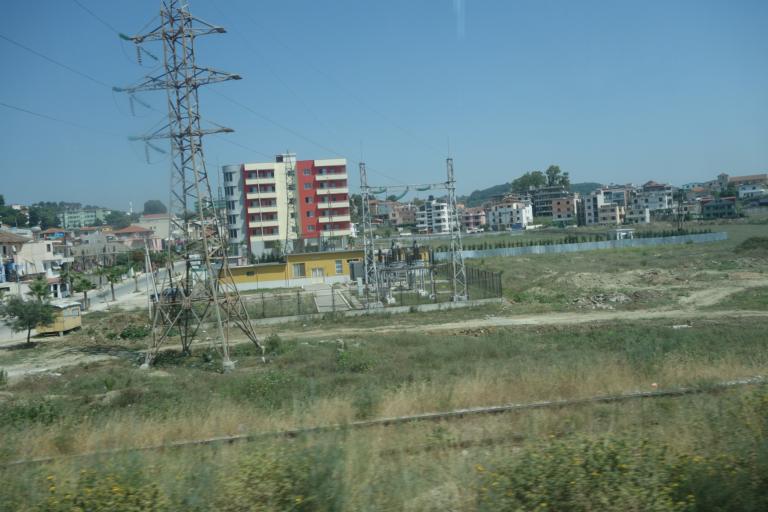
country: AL
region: Tirane
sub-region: Rrethi i Kavajes
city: Golem
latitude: 41.2473
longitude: 19.5257
